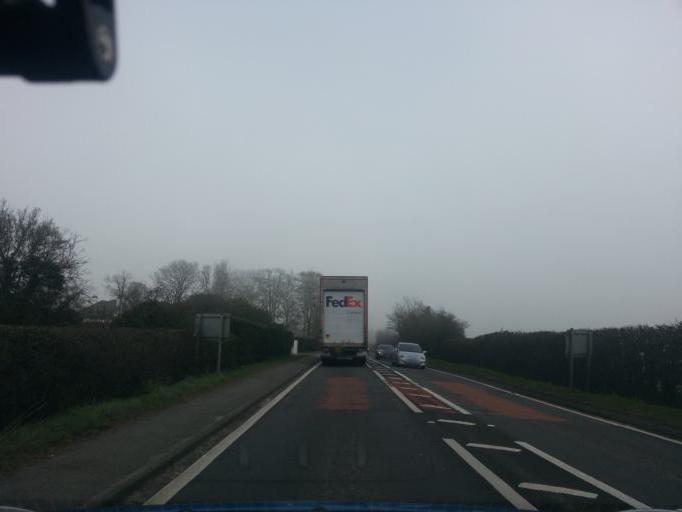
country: GB
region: England
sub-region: Oxfordshire
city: Boars Hill
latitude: 51.7215
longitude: -1.3316
